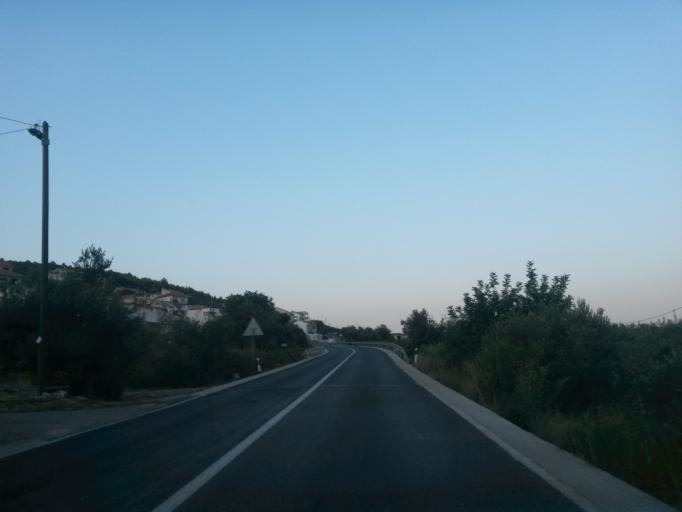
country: HR
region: Splitsko-Dalmatinska
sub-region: Grad Trogir
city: Trogir
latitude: 43.5138
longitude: 16.1843
